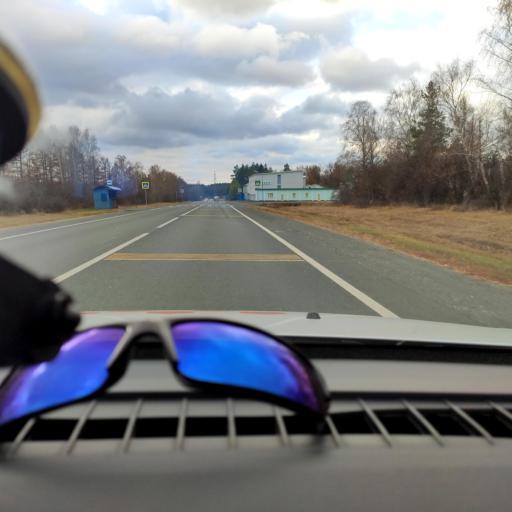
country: RU
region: Samara
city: Volzhskiy
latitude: 53.4570
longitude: 50.1263
